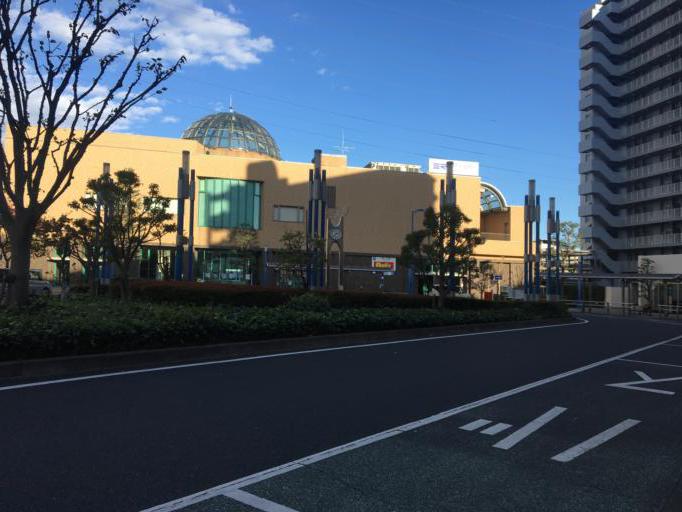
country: JP
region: Saitama
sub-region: Kawaguchi-shi
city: Hatogaya-honcho
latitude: 35.8308
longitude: 139.7352
